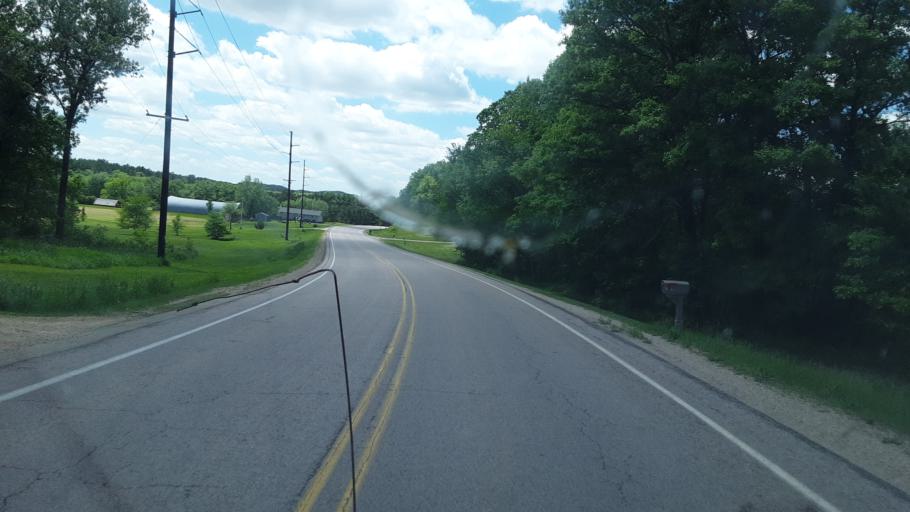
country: US
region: Wisconsin
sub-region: Sauk County
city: Lake Delton
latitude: 43.5910
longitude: -89.8900
